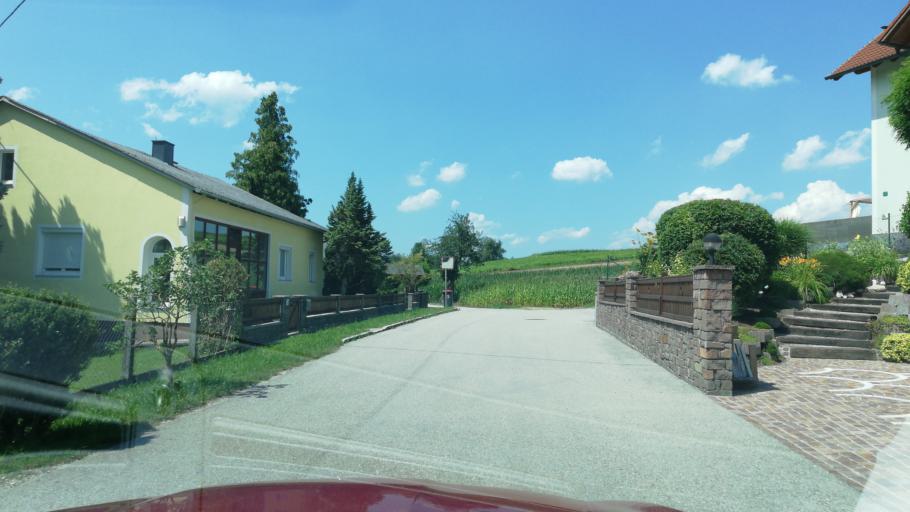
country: AT
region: Upper Austria
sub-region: Wels-Land
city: Buchkirchen
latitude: 48.2190
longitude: 13.9744
